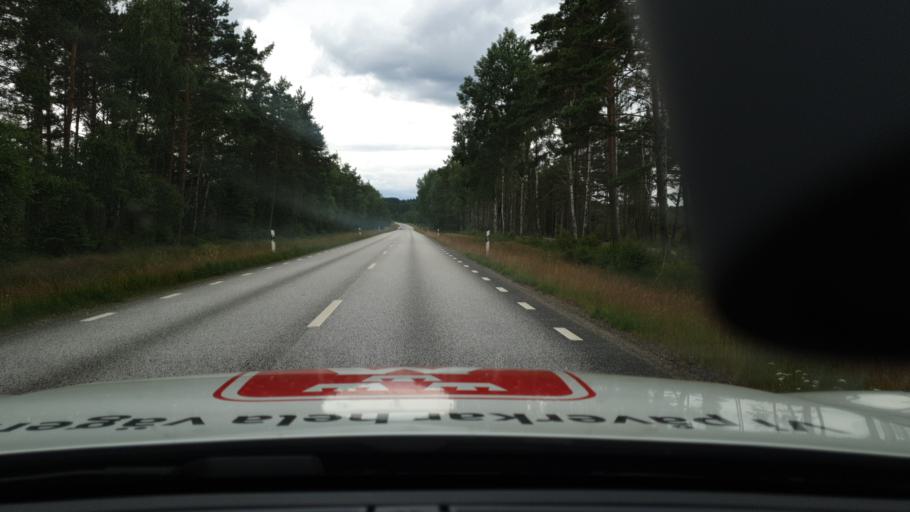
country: SE
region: Joenkoeping
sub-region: Gnosjo Kommun
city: Hillerstorp
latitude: 57.2793
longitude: 13.8117
